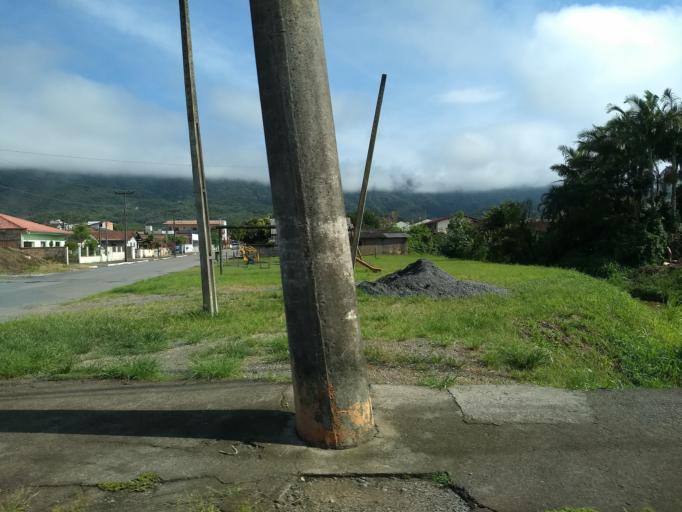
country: BR
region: Santa Catarina
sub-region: Schroeder
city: Schroeder
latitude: -26.4381
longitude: -49.1525
